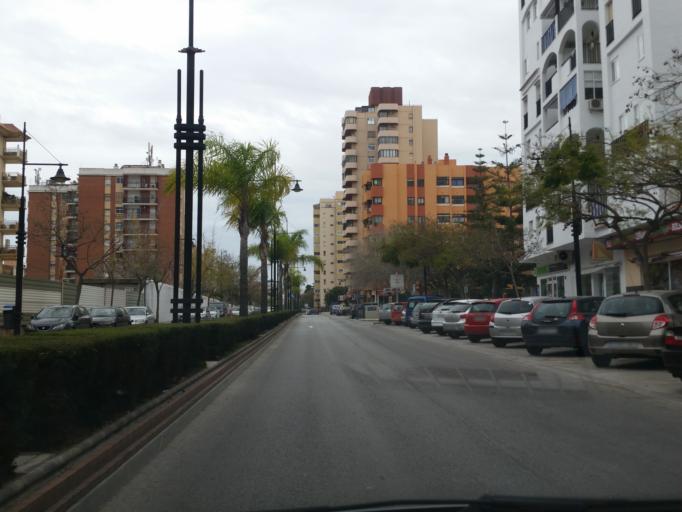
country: ES
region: Andalusia
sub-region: Provincia de Malaga
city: Fuengirola
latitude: 36.5469
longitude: -4.6201
